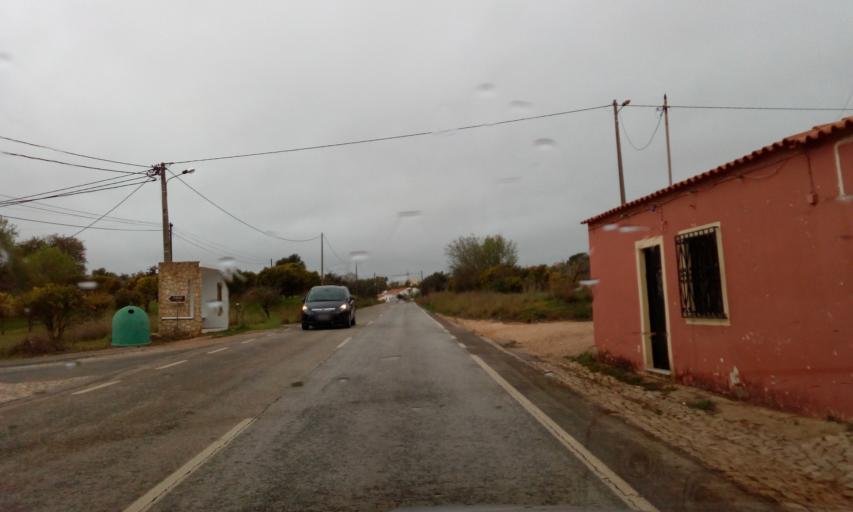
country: PT
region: Faro
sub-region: Albufeira
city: Guia
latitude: 37.1718
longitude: -8.3366
